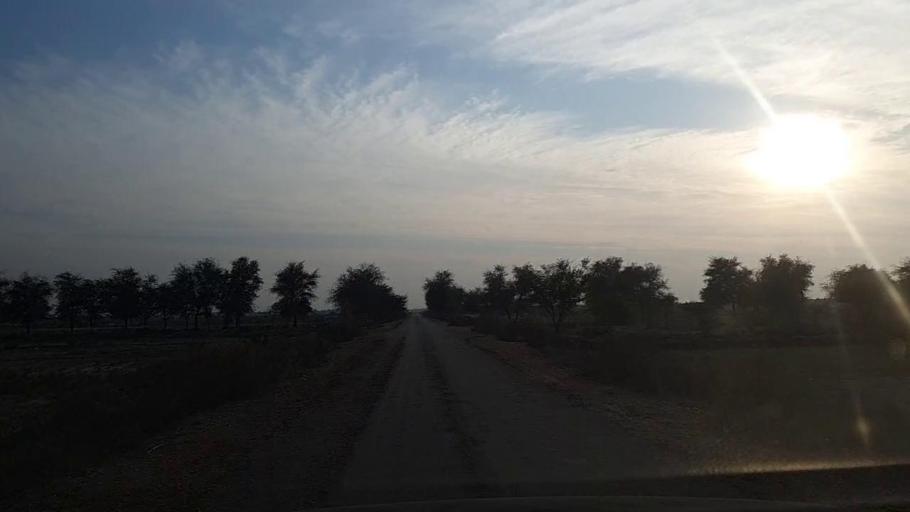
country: PK
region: Sindh
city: Jam Sahib
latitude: 26.4092
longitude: 68.5103
